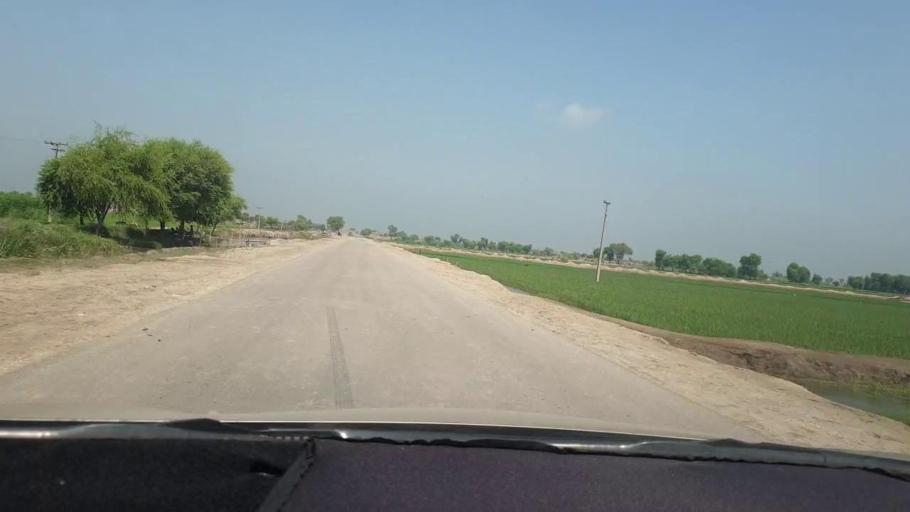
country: PK
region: Sindh
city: Miro Khan
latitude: 27.7802
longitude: 68.0544
